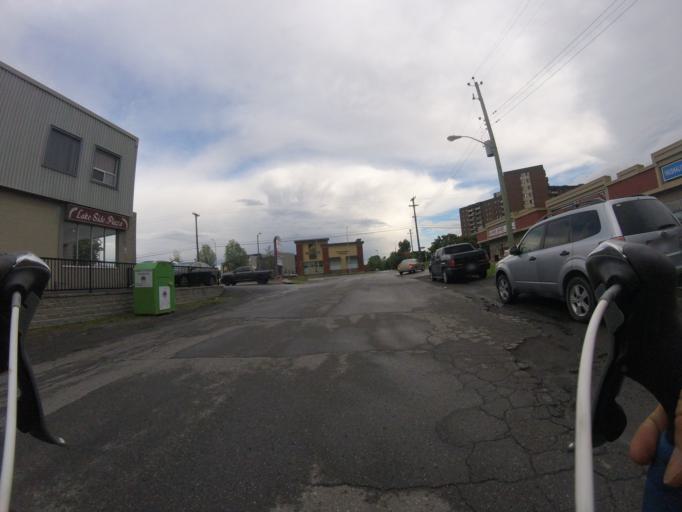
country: CA
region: Ontario
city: Bells Corners
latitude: 45.3550
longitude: -75.8067
